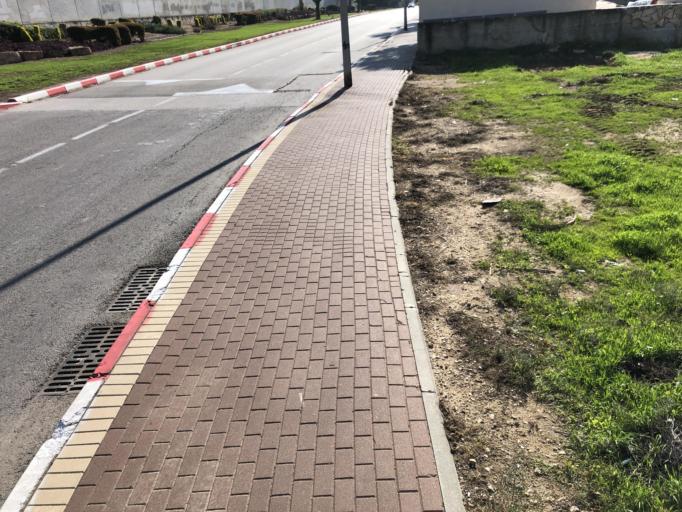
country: IL
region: Northern District
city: `Akko
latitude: 32.9248
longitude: 35.0967
